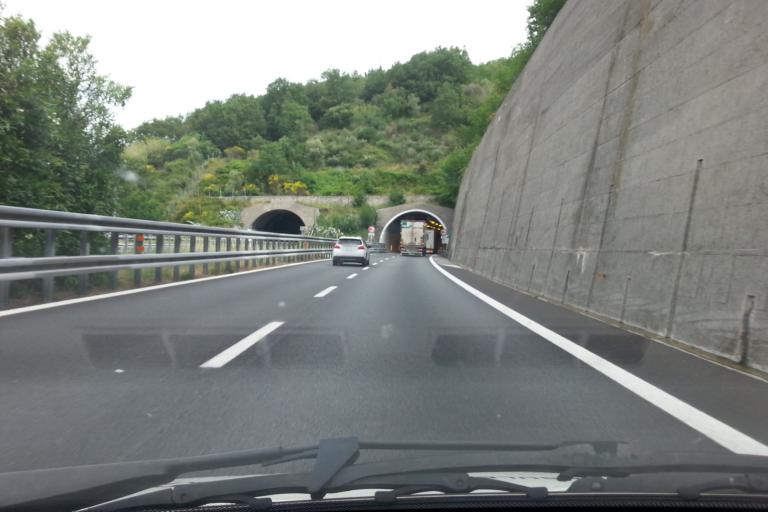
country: IT
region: Liguria
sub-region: Provincia di Savona
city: Calice Ligure
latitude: 44.1972
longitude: 8.3052
